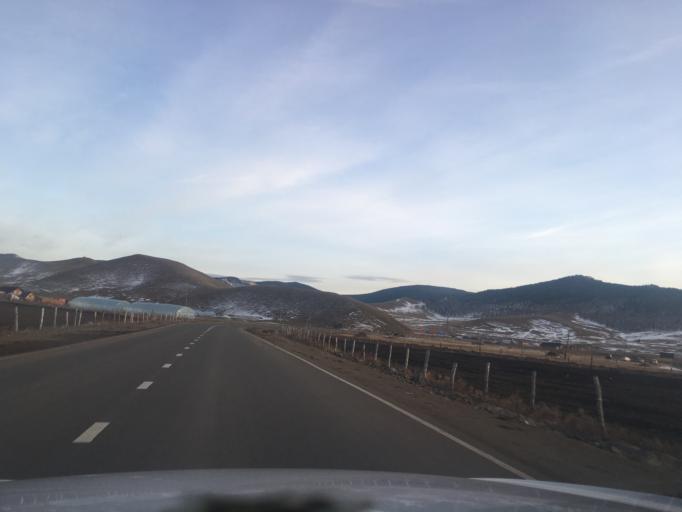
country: MN
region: Ulaanbaatar
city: Ulaanbaatar
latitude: 48.1034
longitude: 106.7358
